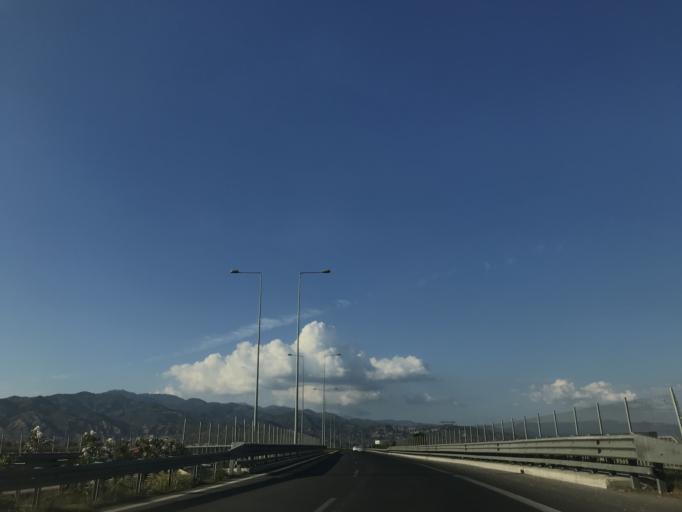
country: TR
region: Aydin
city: Tepecik
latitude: 37.8149
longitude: 27.8633
